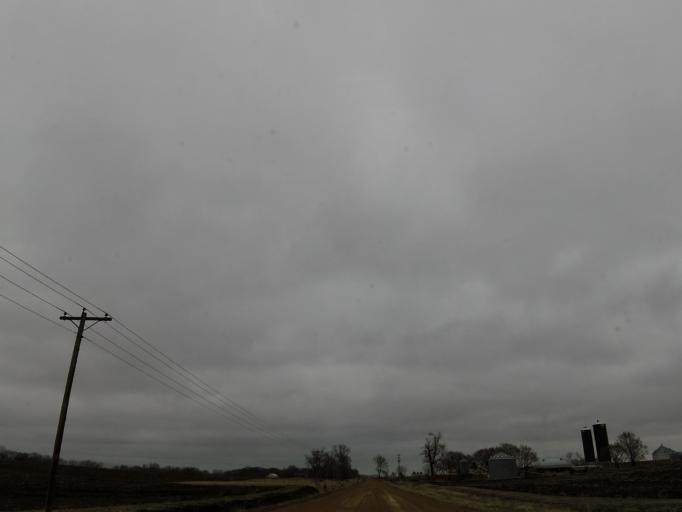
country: US
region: Minnesota
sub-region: Scott County
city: Shakopee
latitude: 44.7032
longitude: -93.5340
